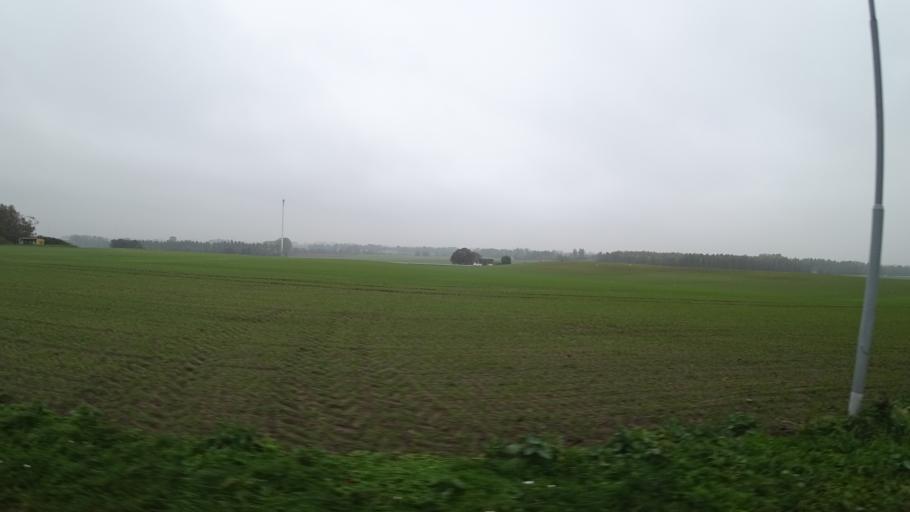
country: SE
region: Skane
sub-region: Kavlinge Kommun
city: Kaevlinge
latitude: 55.7985
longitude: 13.1669
